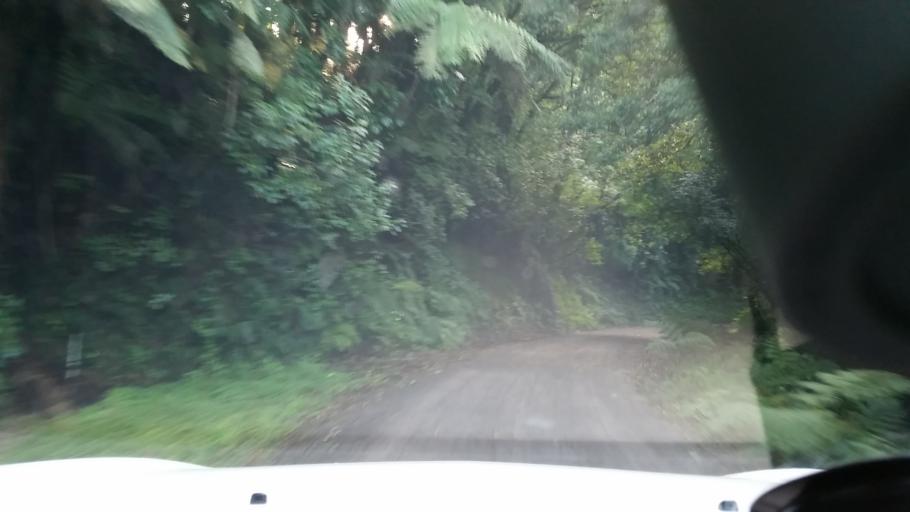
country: NZ
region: Bay of Plenty
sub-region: Kawerau District
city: Kawerau
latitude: -38.0178
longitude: 176.5895
